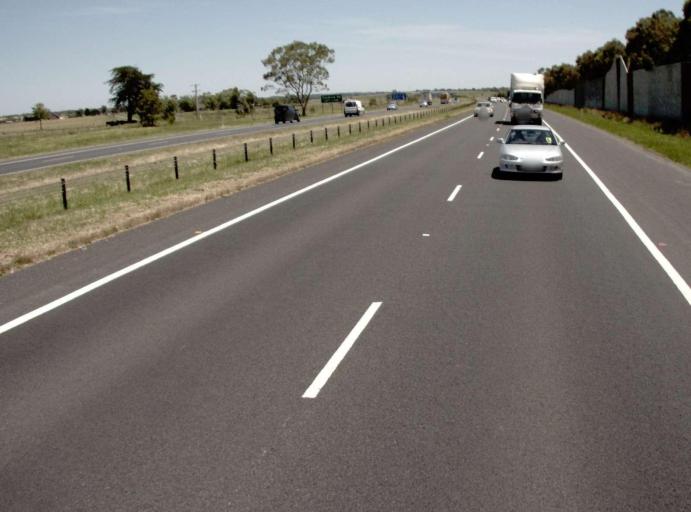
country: AU
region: Victoria
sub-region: Cardinia
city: Officer
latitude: -38.0834
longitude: 145.4465
